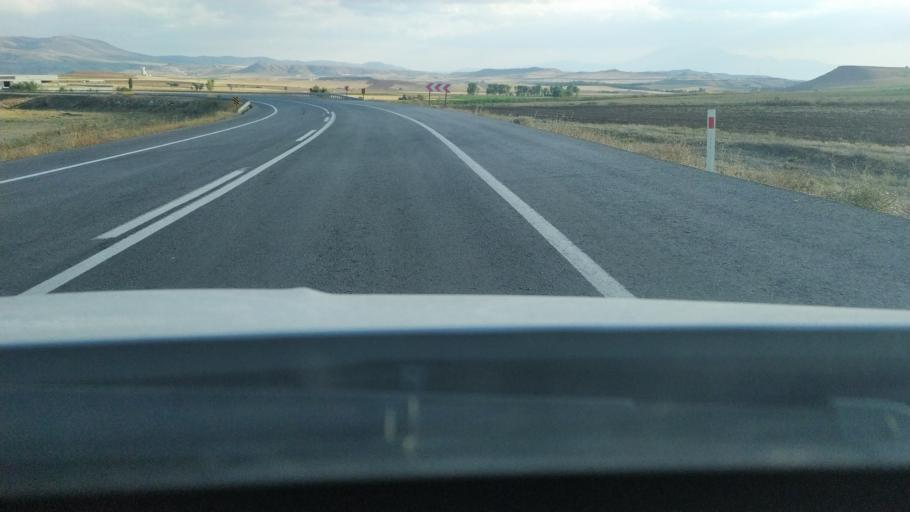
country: TR
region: Kayseri
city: Muncusun
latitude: 38.9190
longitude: 35.7504
